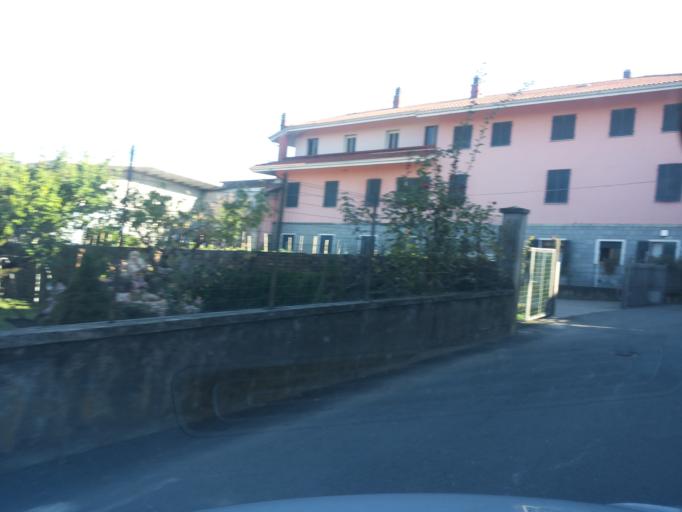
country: IT
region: Piedmont
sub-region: Provincia di Torino
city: Strambino
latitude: 45.3988
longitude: 7.8952
